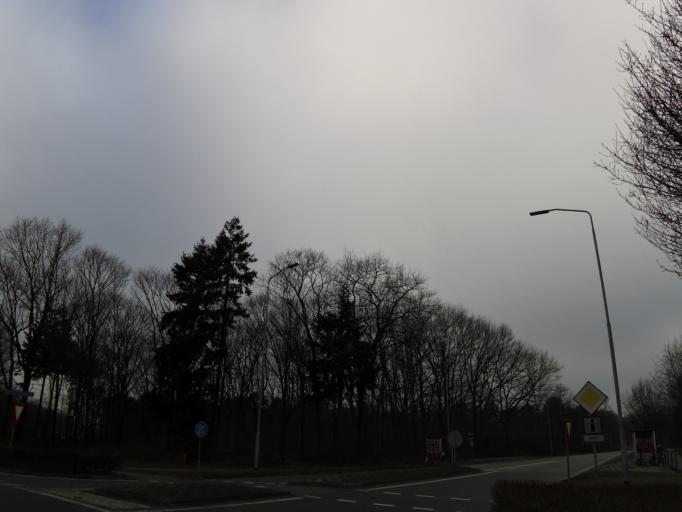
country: NL
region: North Brabant
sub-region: Gemeente Mill en Sint Hubert
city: Wilbertoord
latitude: 51.6743
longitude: 5.7993
